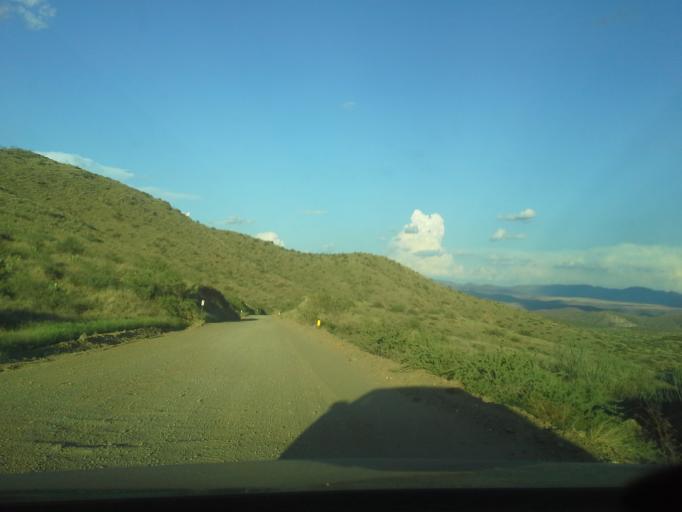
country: US
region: Arizona
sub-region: Yavapai County
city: Spring Valley
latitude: 34.2769
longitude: -112.2521
